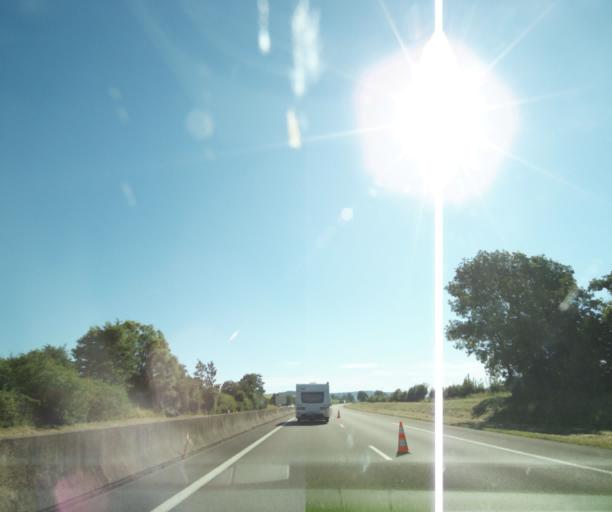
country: FR
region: Champagne-Ardenne
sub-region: Departement de la Haute-Marne
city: Nogent-le-Bas
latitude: 47.9529
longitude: 5.3586
